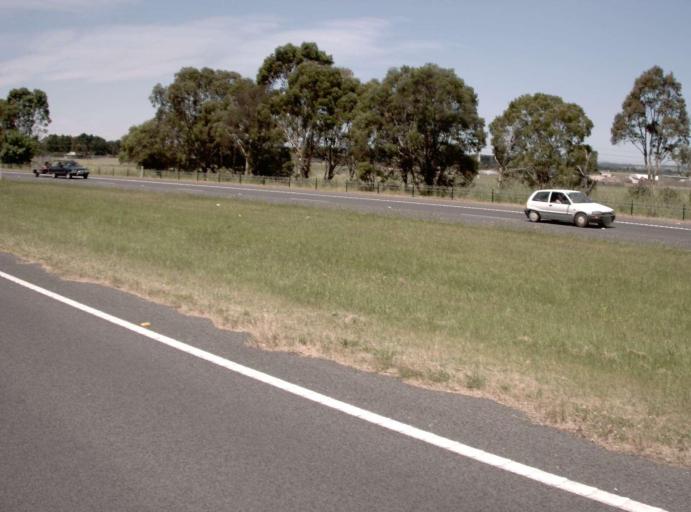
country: AU
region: Victoria
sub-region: Latrobe
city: Morwell
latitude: -38.2443
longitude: 146.4396
